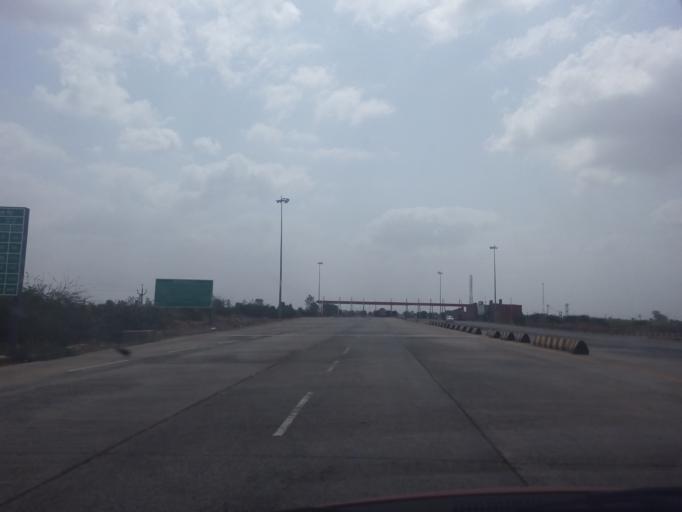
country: IN
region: Gujarat
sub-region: Surendranagar
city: Dhrangadhra
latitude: 23.0013
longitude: 71.3700
